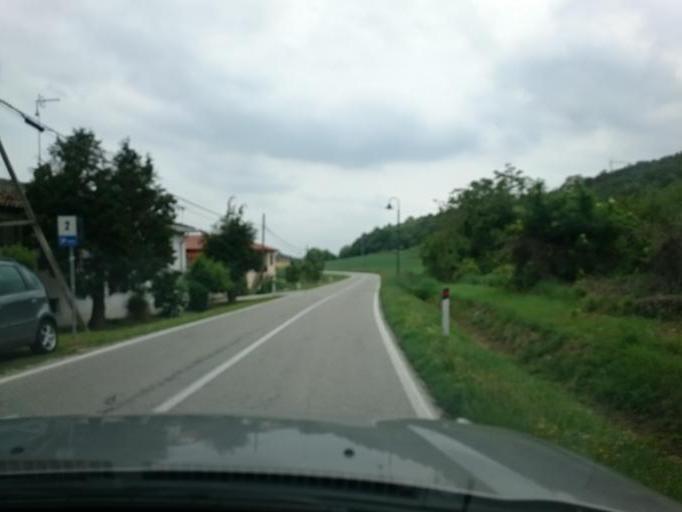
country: IT
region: Veneto
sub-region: Provincia di Padova
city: Arqua Petrarca
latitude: 45.2652
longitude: 11.7200
